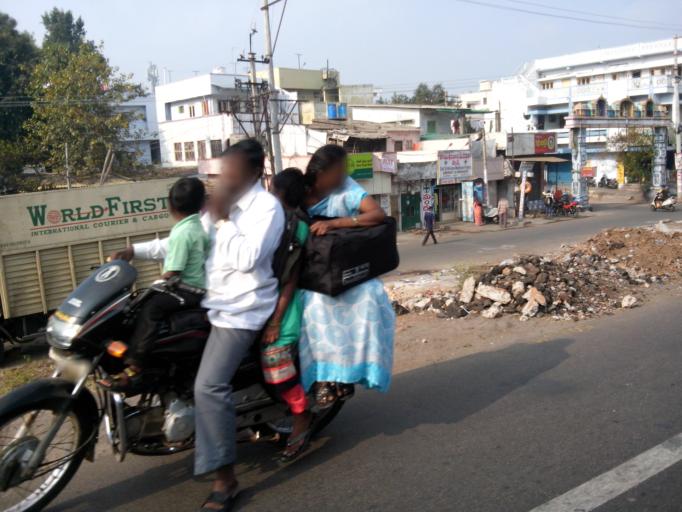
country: IN
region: Andhra Pradesh
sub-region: Krishna
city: Vijayawada
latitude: 16.5074
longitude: 80.6248
